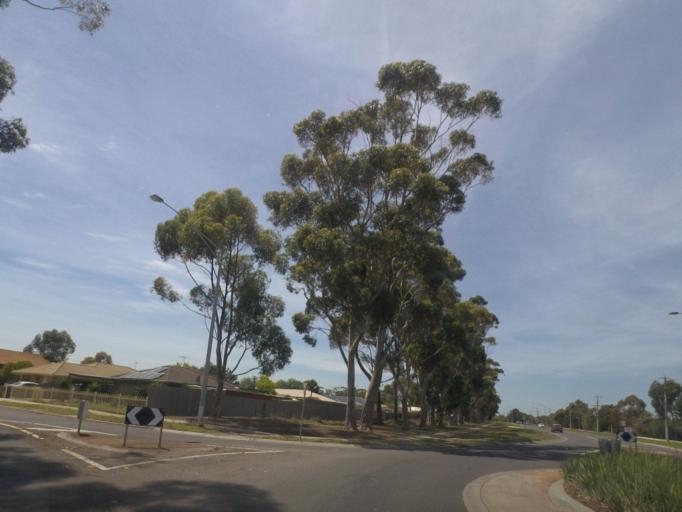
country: AU
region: Victoria
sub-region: Wyndham
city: Werribee
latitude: -37.8837
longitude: 144.6235
